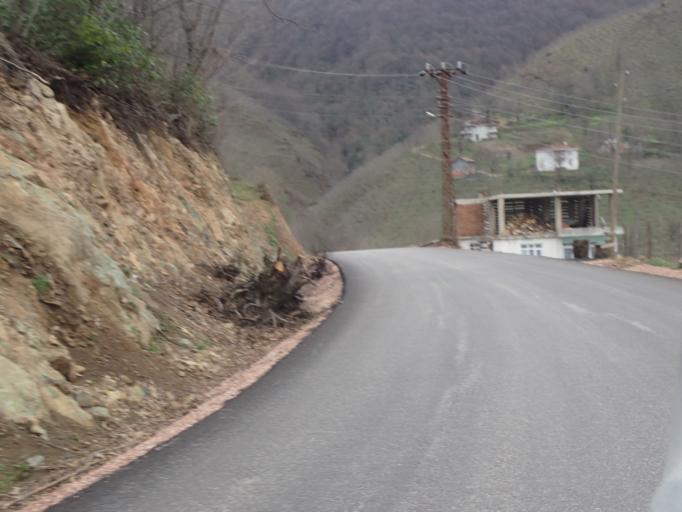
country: TR
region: Ordu
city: Camas
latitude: 40.8850
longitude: 37.5197
